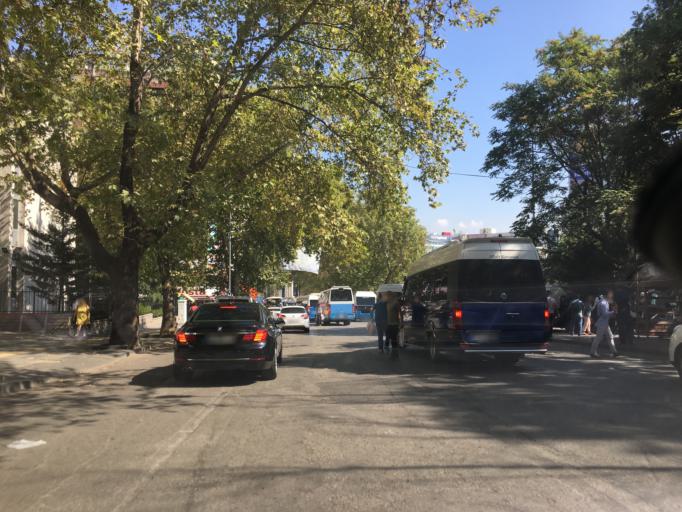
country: TR
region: Ankara
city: Ankara
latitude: 39.9187
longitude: 32.8519
